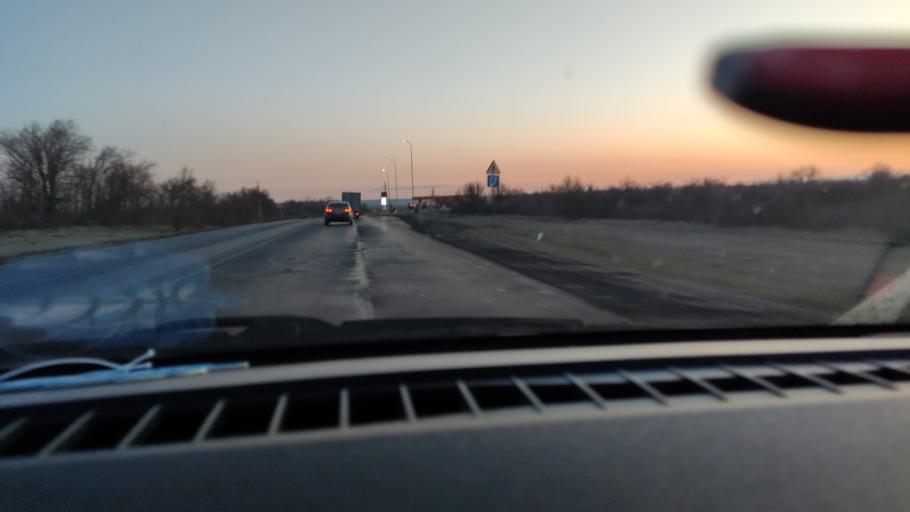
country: RU
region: Saratov
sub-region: Saratovskiy Rayon
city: Saratov
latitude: 51.6789
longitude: 46.0013
